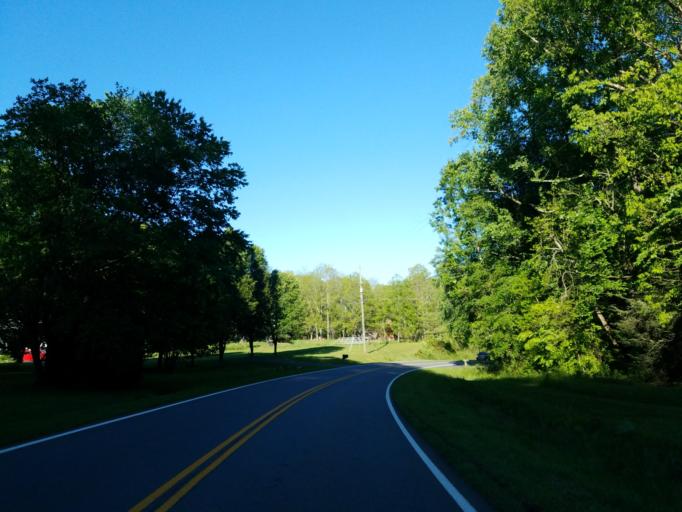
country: US
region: Georgia
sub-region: Gilmer County
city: Ellijay
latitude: 34.6754
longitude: -84.3412
